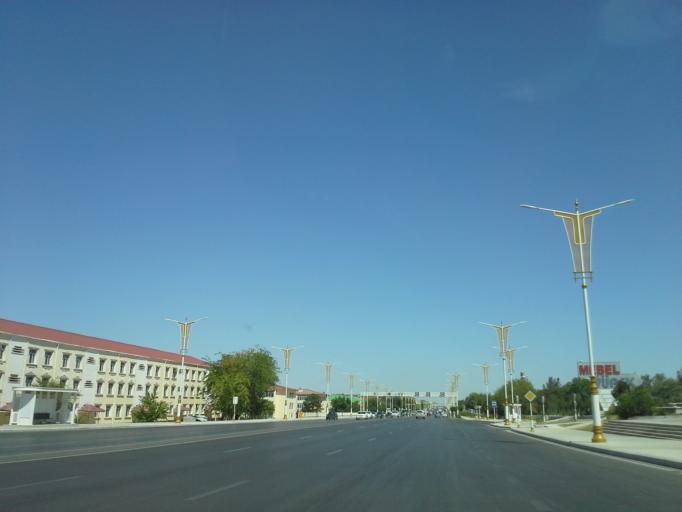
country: TM
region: Ahal
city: Ashgabat
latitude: 37.9101
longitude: 58.4065
